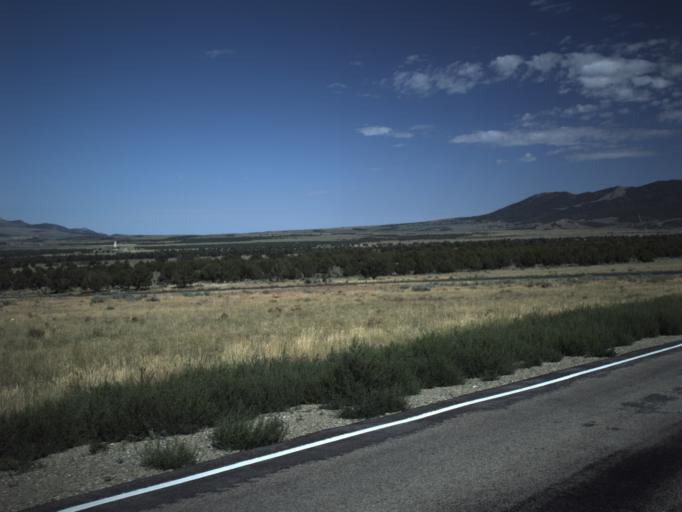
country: US
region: Utah
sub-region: Utah County
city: Genola
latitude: 39.9270
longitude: -112.1473
